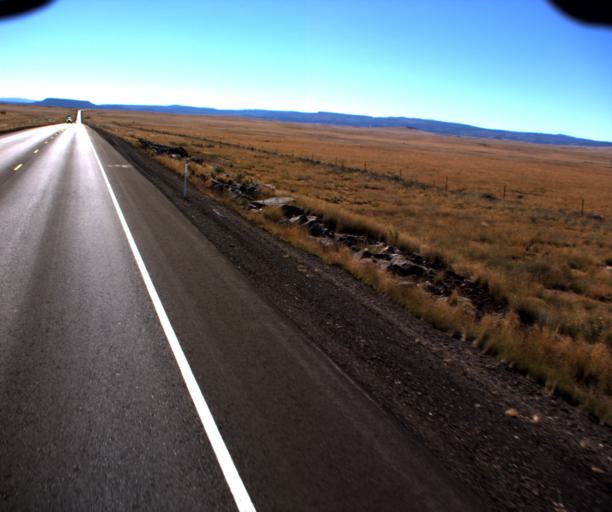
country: US
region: Arizona
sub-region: Apache County
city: Springerville
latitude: 34.2244
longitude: -109.3376
